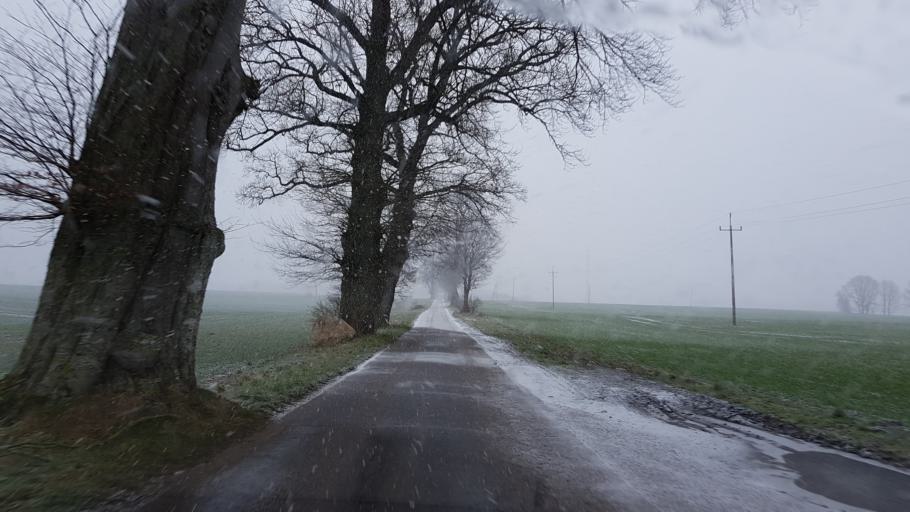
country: PL
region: West Pomeranian Voivodeship
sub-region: Powiat slawienski
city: Slawno
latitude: 54.2716
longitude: 16.6486
